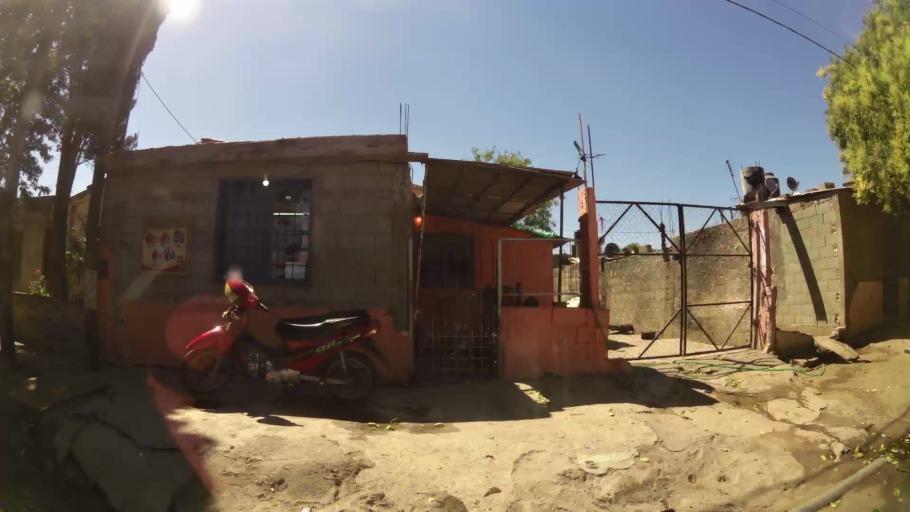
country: AR
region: Cordoba
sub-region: Departamento de Capital
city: Cordoba
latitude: -31.4077
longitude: -64.1386
